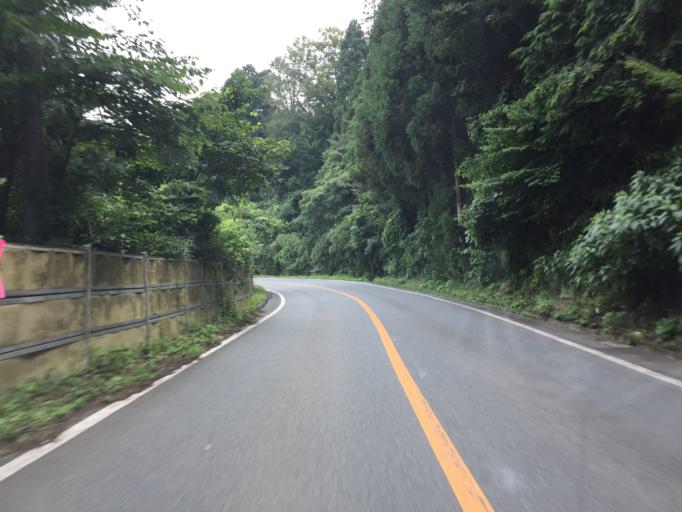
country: JP
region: Fukushima
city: Namie
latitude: 37.6015
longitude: 140.9101
